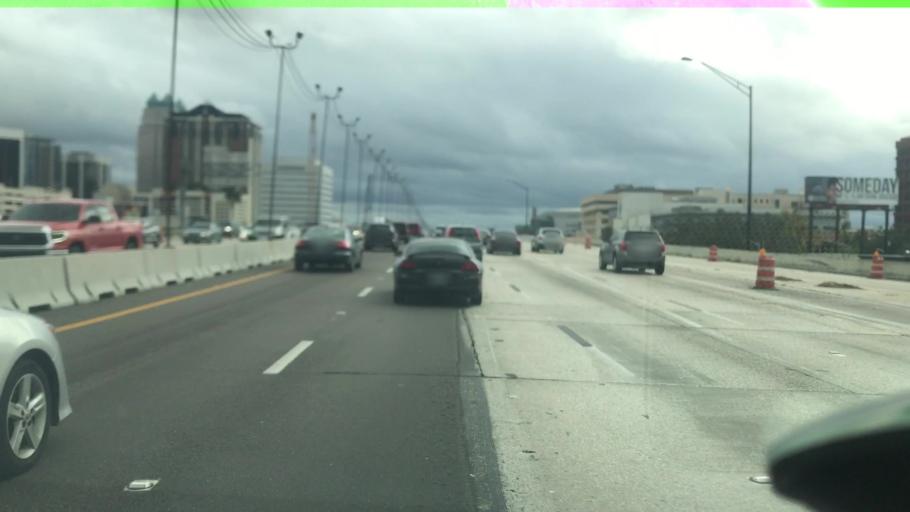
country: US
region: Florida
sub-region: Orange County
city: Orlando
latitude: 28.5473
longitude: -81.3825
